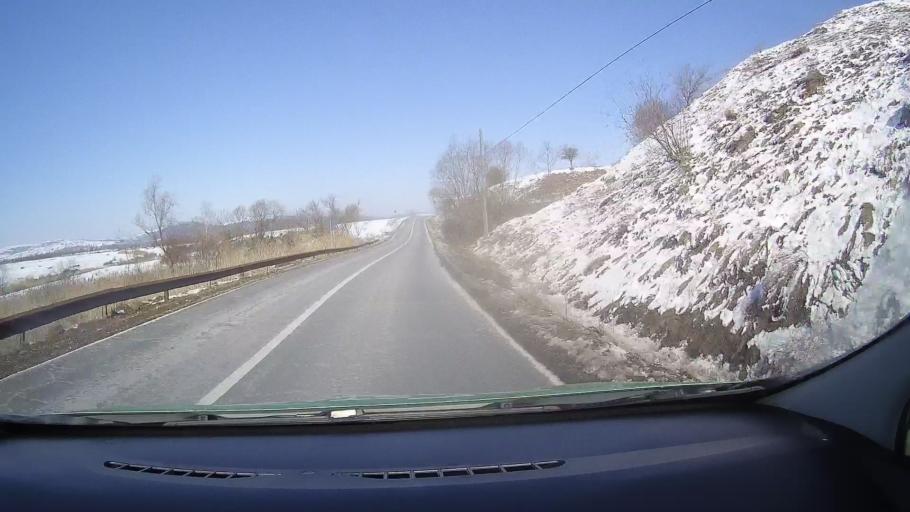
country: RO
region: Brasov
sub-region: Comuna Comana
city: Comana de Jos
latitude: 45.9008
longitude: 25.2270
